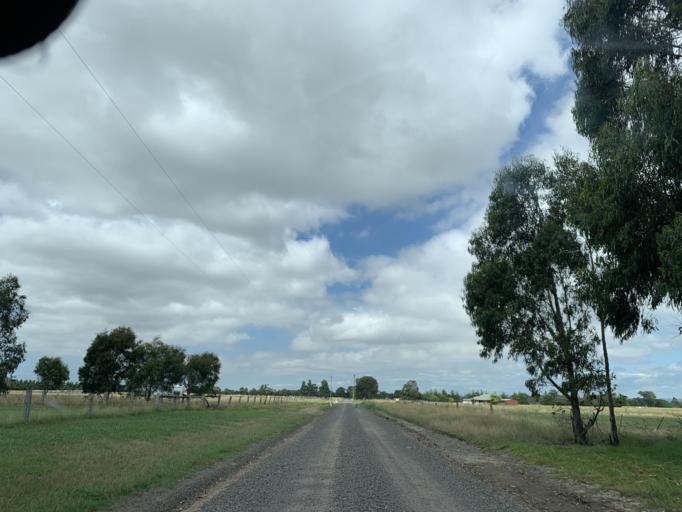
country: AU
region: Victoria
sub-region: Latrobe
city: Traralgon
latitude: -38.1146
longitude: 146.5629
